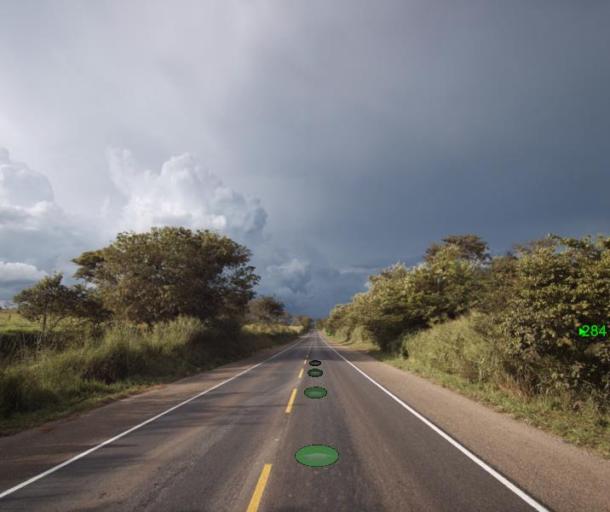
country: BR
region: Goias
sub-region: Ceres
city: Ceres
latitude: -15.1678
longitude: -49.5430
